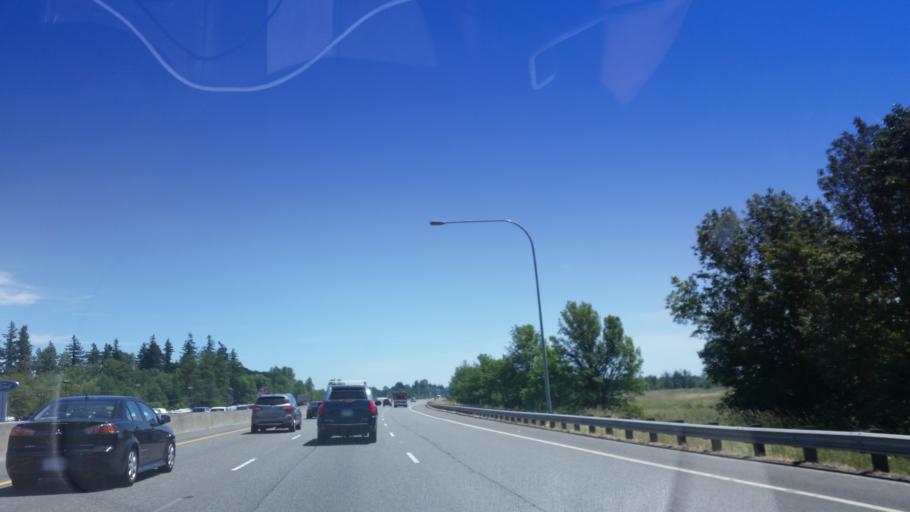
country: US
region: Washington
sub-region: Lewis County
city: Chehalis
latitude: 46.6434
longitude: -122.9542
